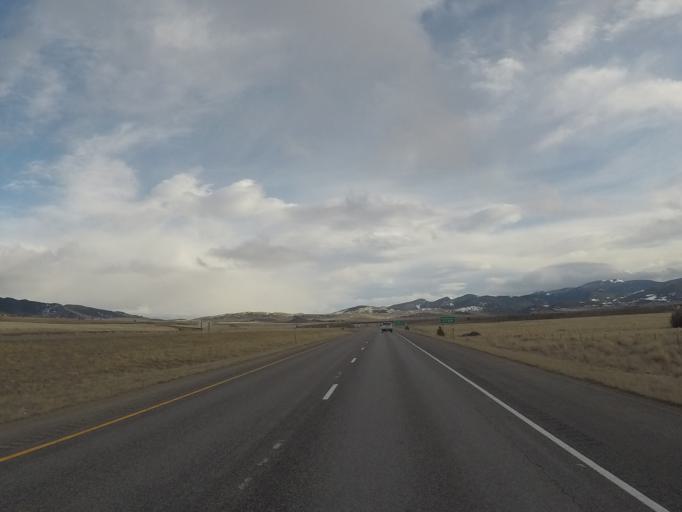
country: US
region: Montana
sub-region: Deer Lodge County
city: Warm Springs
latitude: 46.1039
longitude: -112.7958
